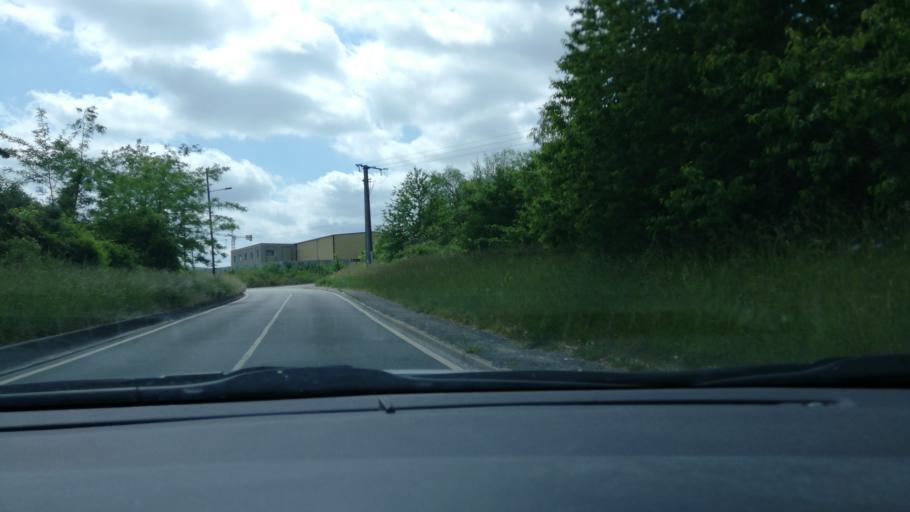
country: FR
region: Ile-de-France
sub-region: Departement du Val-d'Oise
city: Vaureal
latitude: 49.0671
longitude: 2.0231
